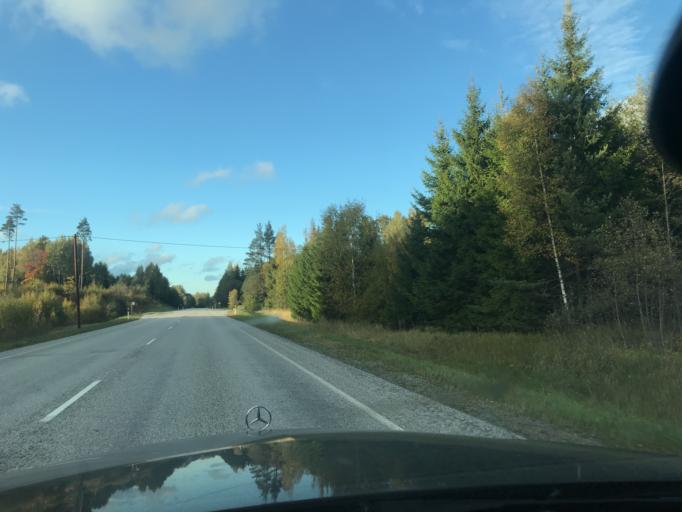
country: RU
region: Pskov
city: Pechory
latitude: 57.6728
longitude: 27.3280
